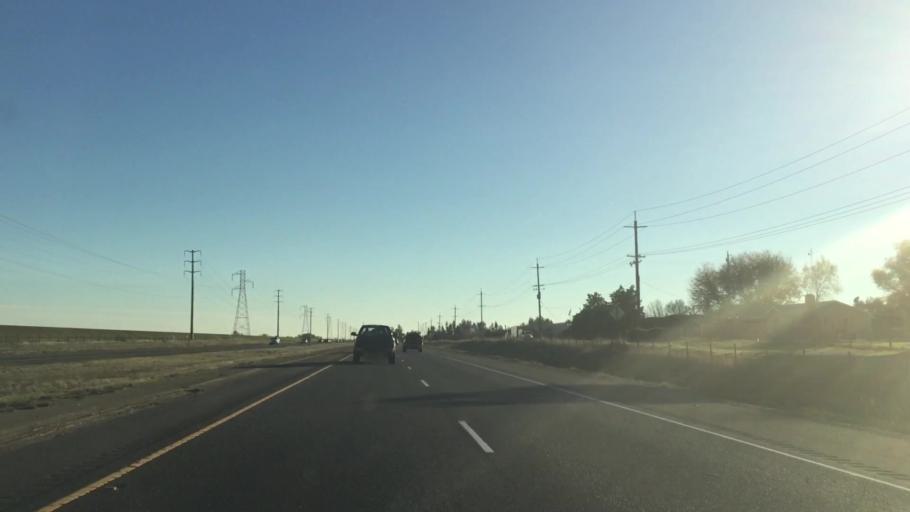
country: US
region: California
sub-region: Yuba County
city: Plumas Lake
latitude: 39.0431
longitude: -121.5433
